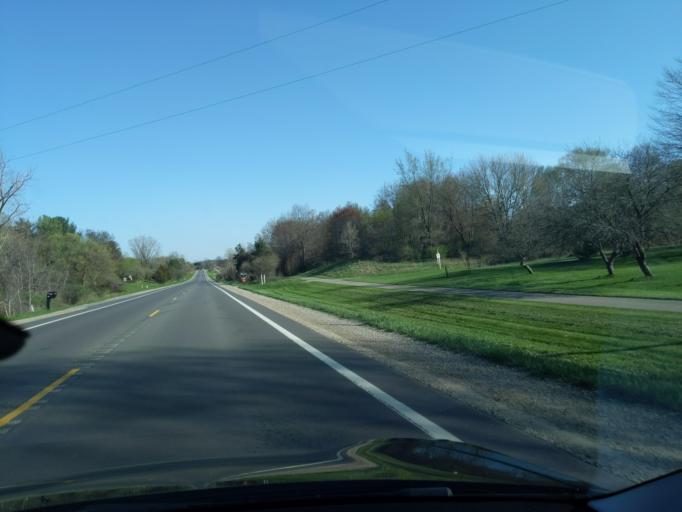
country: US
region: Michigan
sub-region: Washtenaw County
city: Chelsea
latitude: 42.3601
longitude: -84.0610
